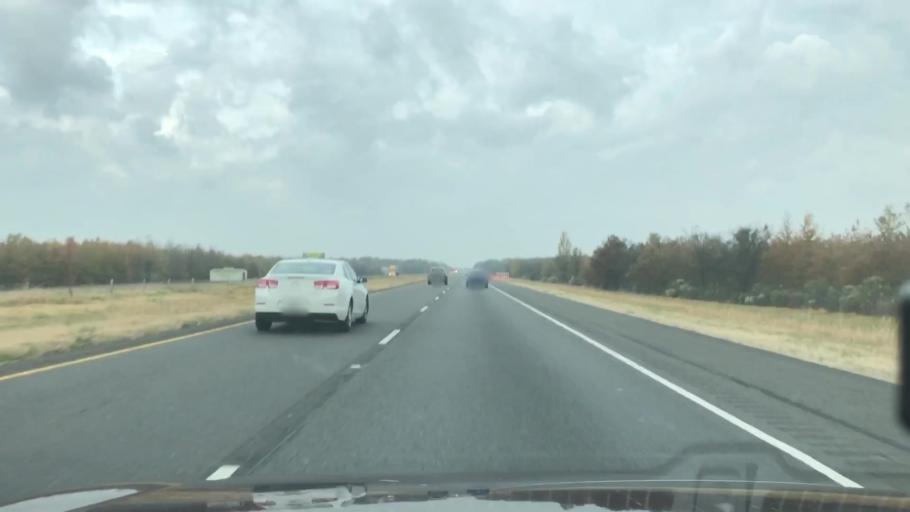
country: US
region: Louisiana
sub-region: Richland Parish
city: Delhi
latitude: 32.4378
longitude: -91.4606
